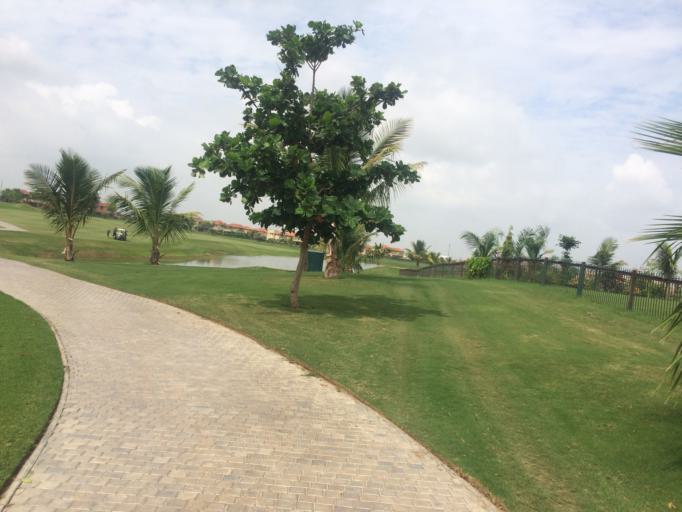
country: IN
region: Gujarat
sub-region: Ahmadabad
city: Sanand
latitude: 23.0225
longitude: 72.3584
